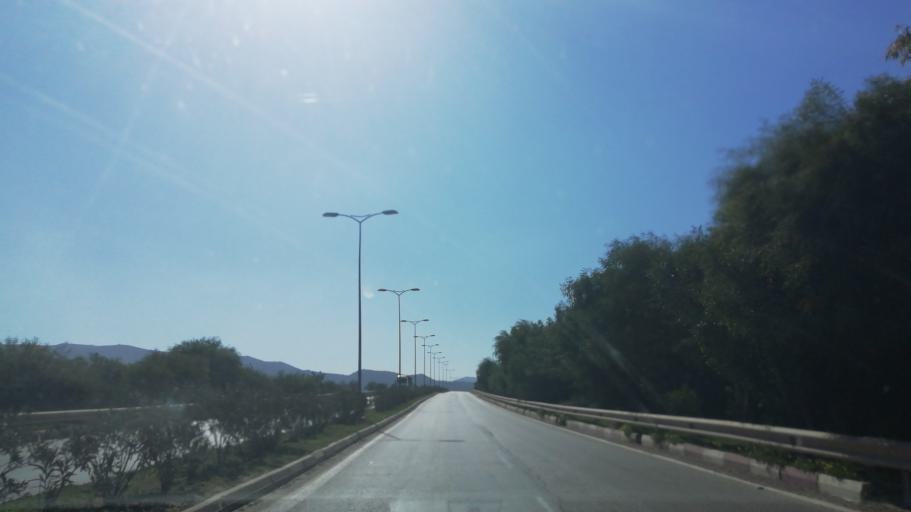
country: DZ
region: Mascara
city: Sig
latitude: 35.5415
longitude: -0.2043
